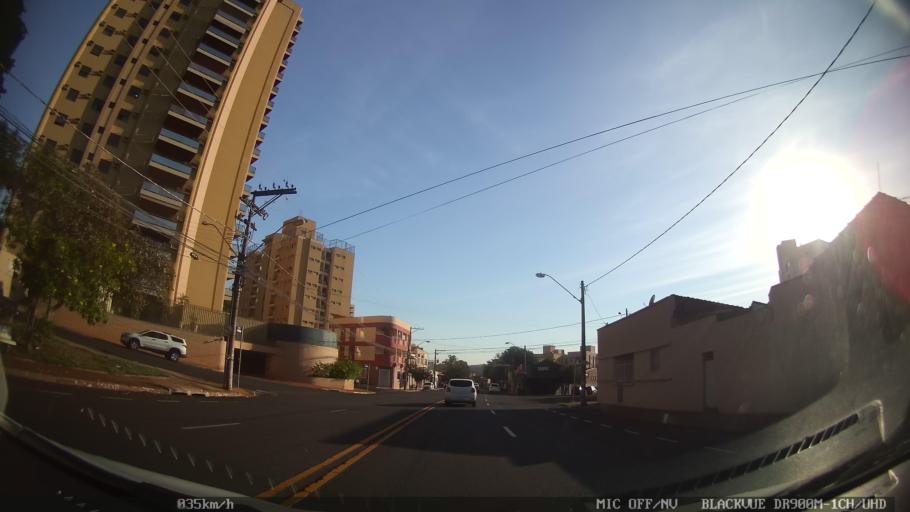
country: BR
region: Sao Paulo
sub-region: Ribeirao Preto
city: Ribeirao Preto
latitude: -21.1888
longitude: -47.8012
